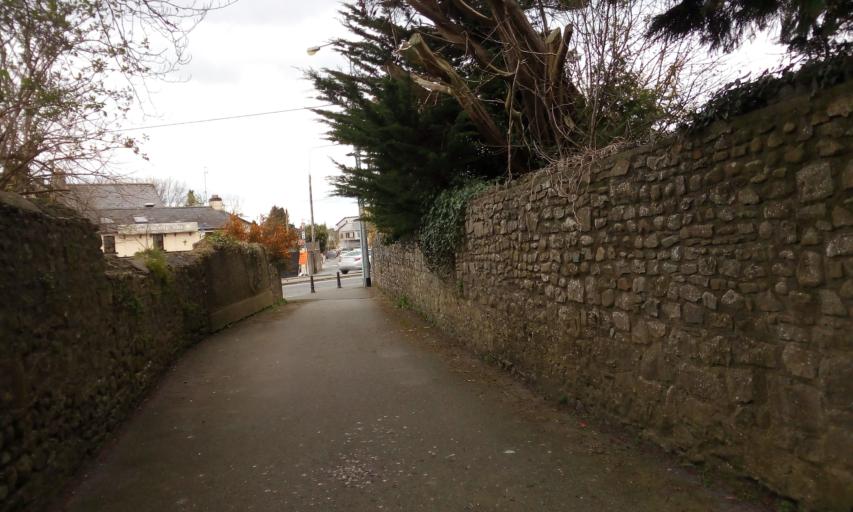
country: IE
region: Leinster
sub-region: Kilkenny
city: Kilkenny
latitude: 52.6441
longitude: -7.2605
